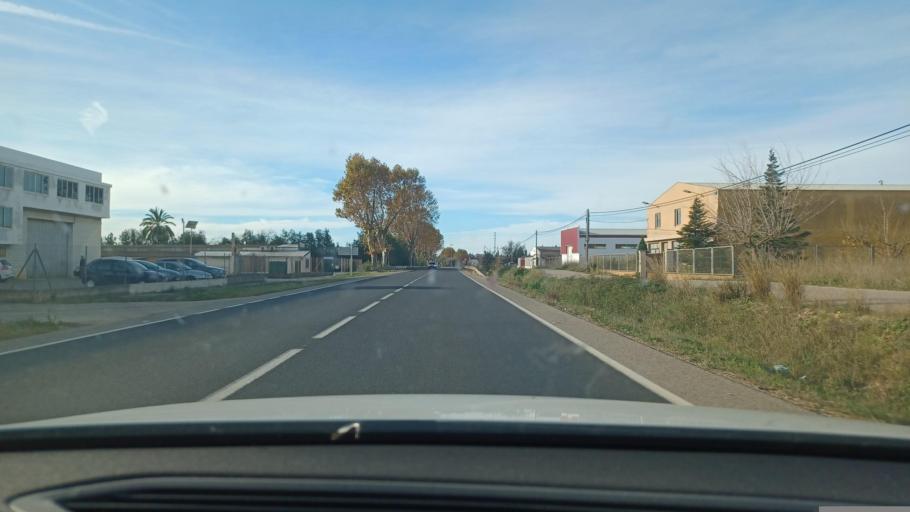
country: ES
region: Catalonia
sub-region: Provincia de Tarragona
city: Ulldecona
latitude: 40.6061
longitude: 0.4577
